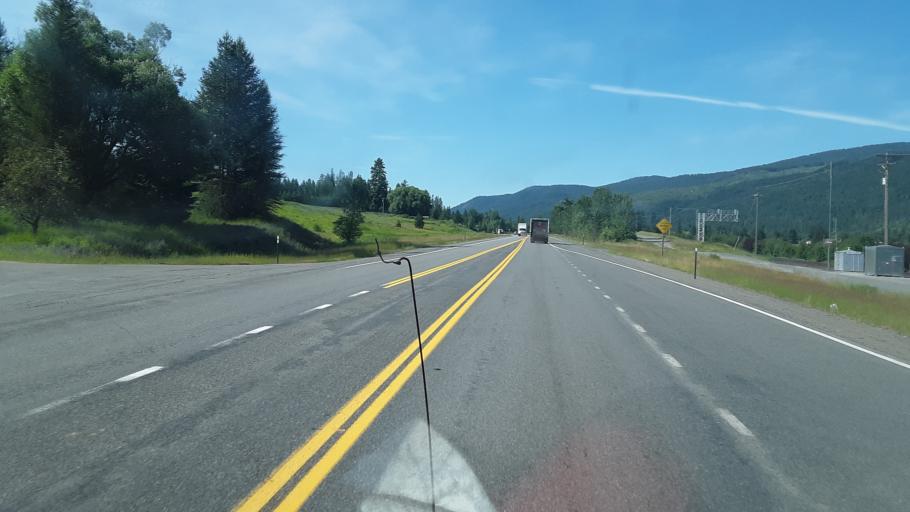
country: US
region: Idaho
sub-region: Bonner County
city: Ponderay
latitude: 48.4076
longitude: -116.5263
